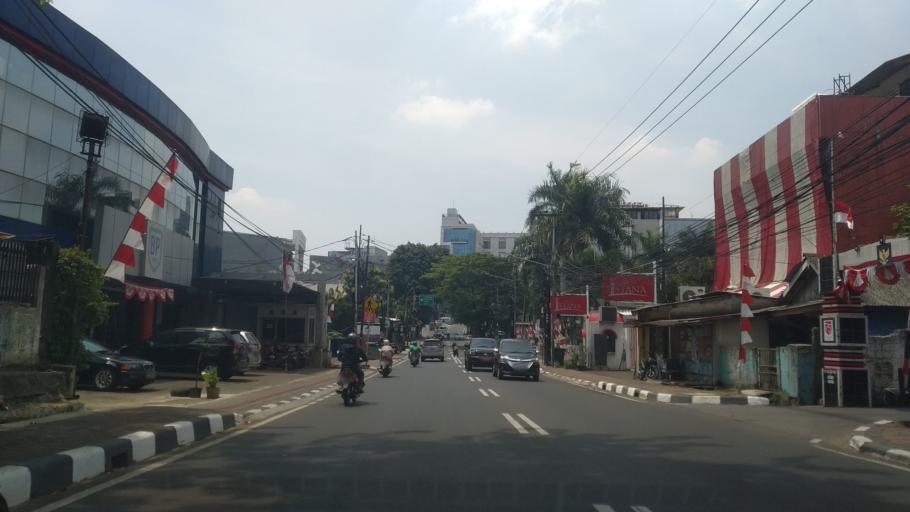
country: ID
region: Banten
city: South Tangerang
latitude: -6.2533
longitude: 106.7759
